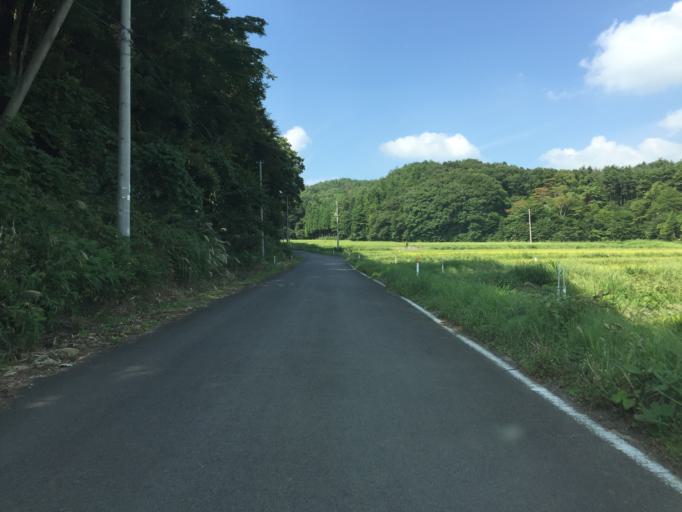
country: JP
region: Fukushima
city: Nihommatsu
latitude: 37.6016
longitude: 140.3832
